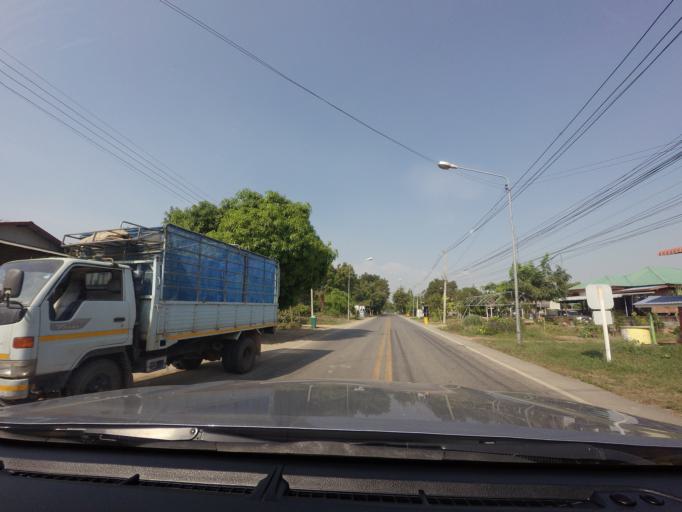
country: TH
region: Sukhothai
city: Kong Krailat
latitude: 16.8548
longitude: 99.9367
